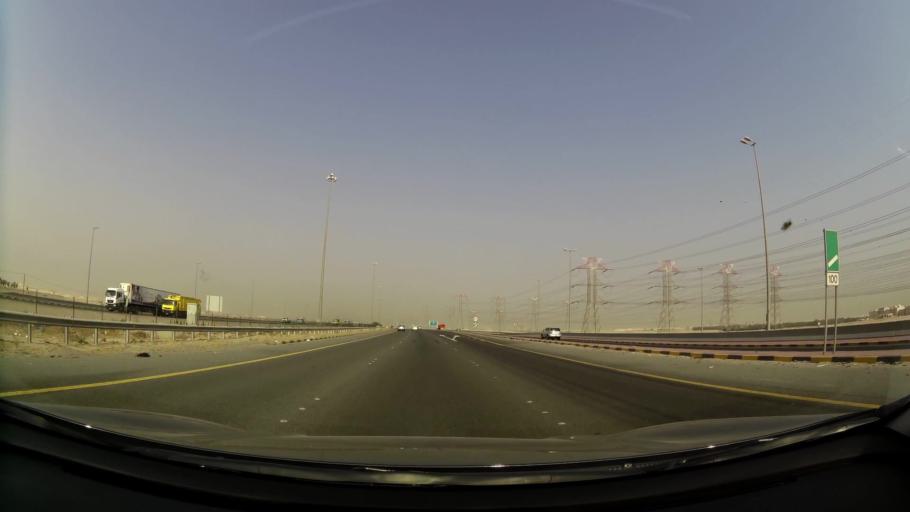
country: KW
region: Al Asimah
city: Ar Rabiyah
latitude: 29.2453
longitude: 47.8757
